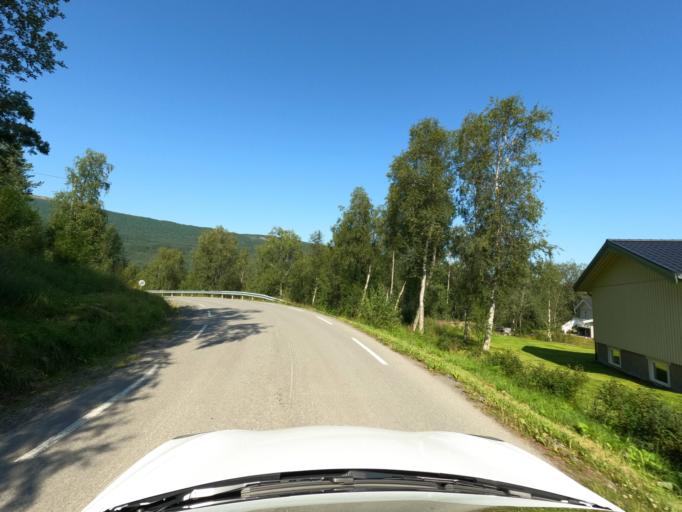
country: NO
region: Nordland
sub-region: Ballangen
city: Ballangen
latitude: 68.3435
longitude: 16.8199
